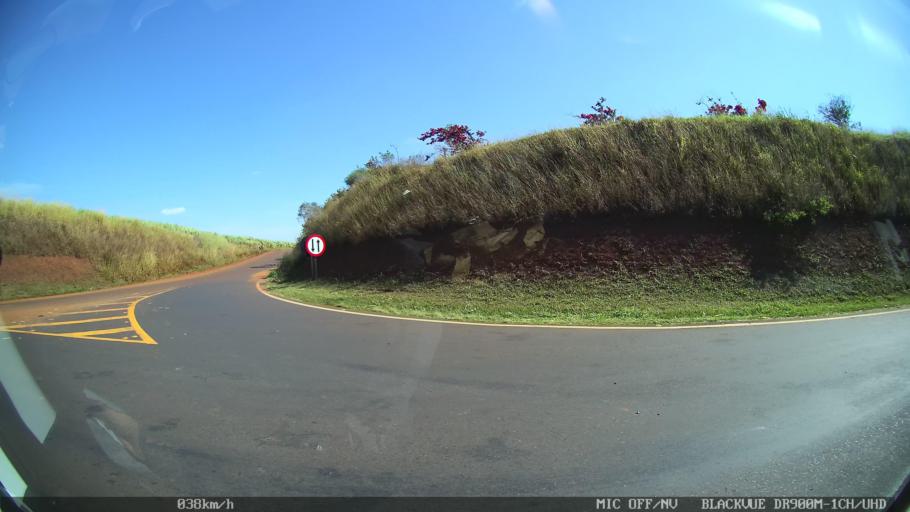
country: BR
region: Sao Paulo
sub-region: Franca
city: Franca
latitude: -20.6766
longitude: -47.4964
